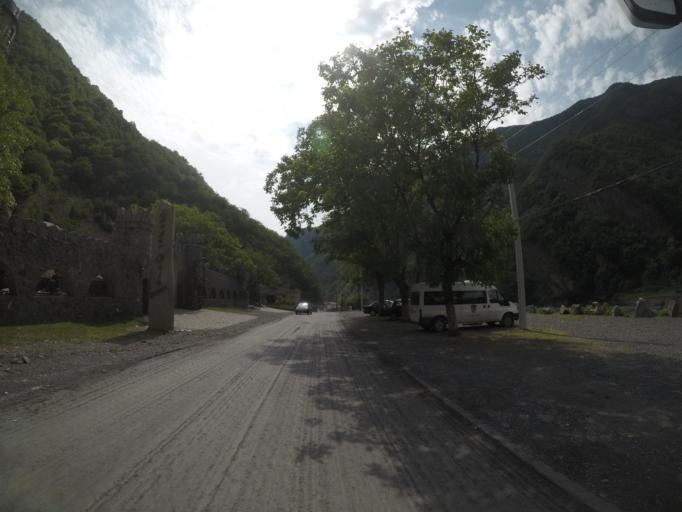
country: AZ
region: Qakh Rayon
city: Qaxbas
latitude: 41.4644
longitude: 47.0389
